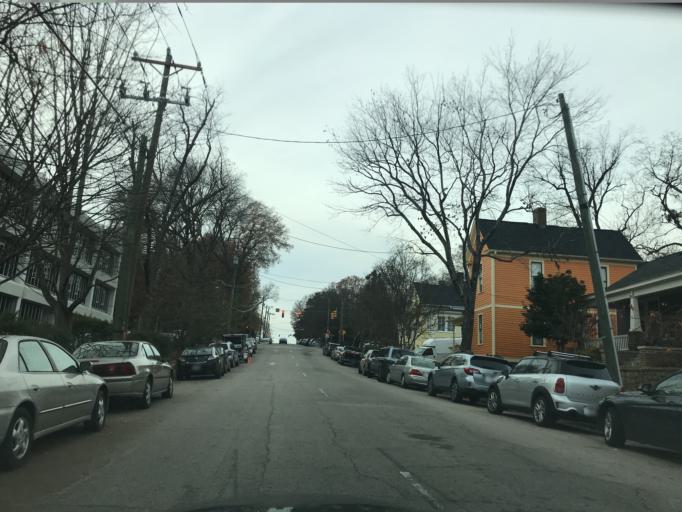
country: US
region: North Carolina
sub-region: Wake County
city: Raleigh
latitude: 35.7837
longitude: -78.6336
